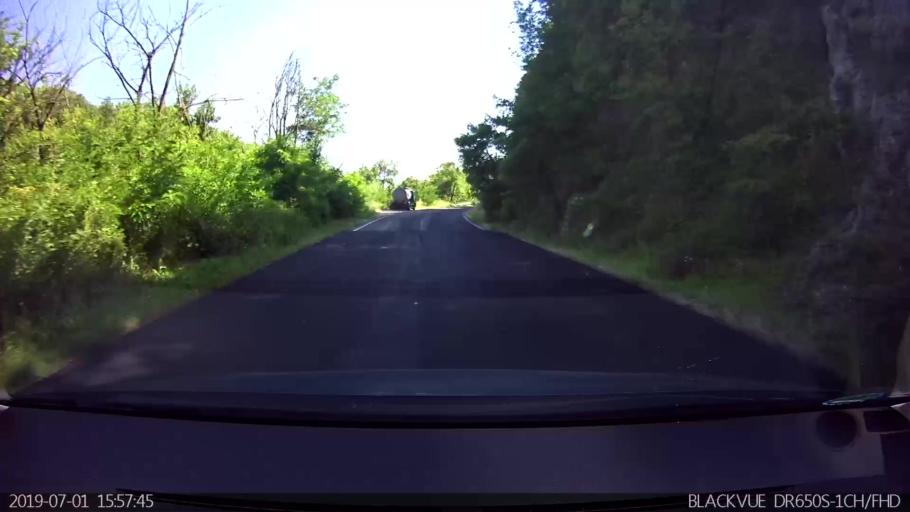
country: IT
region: Latium
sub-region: Provincia di Frosinone
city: Sant'Angelo in Villa-Giglio
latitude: 41.6735
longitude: 13.4216
